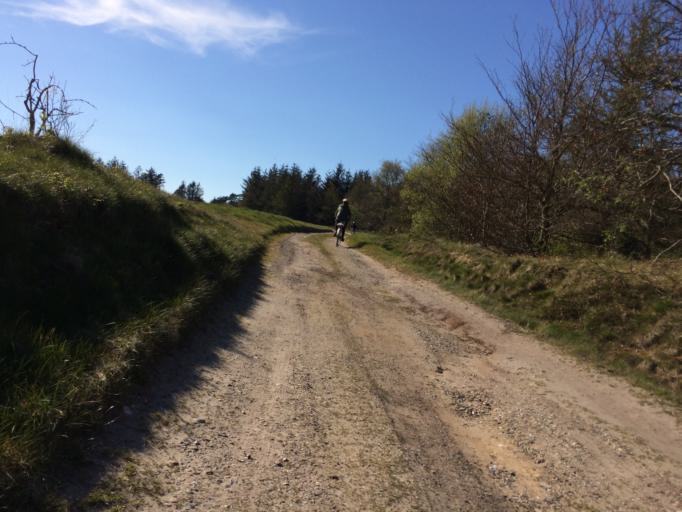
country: DK
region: Central Jutland
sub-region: Struer Kommune
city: Struer
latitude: 56.5418
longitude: 8.6287
